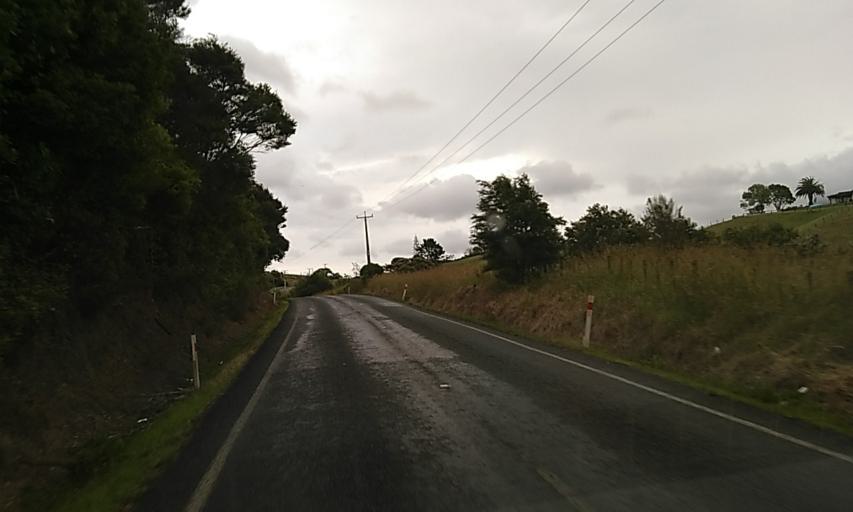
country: NZ
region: Auckland
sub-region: Auckland
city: Pukekohe East
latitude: -37.3019
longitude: 174.9386
